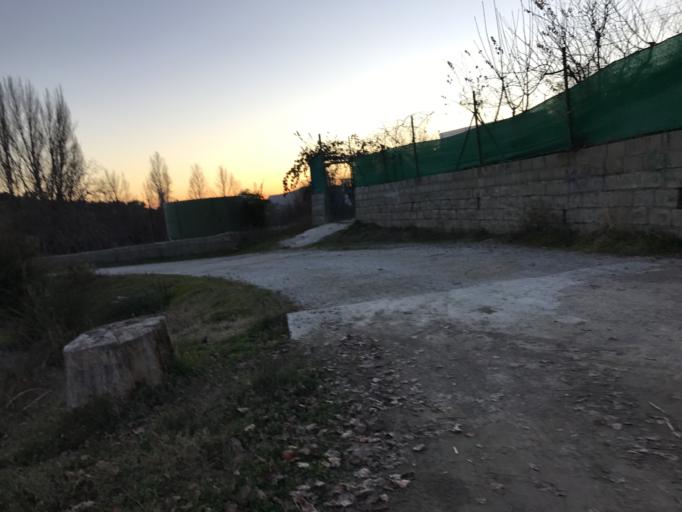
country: ES
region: Andalusia
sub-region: Provincia de Granada
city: Beas de Granada
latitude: 37.2274
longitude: -3.4758
